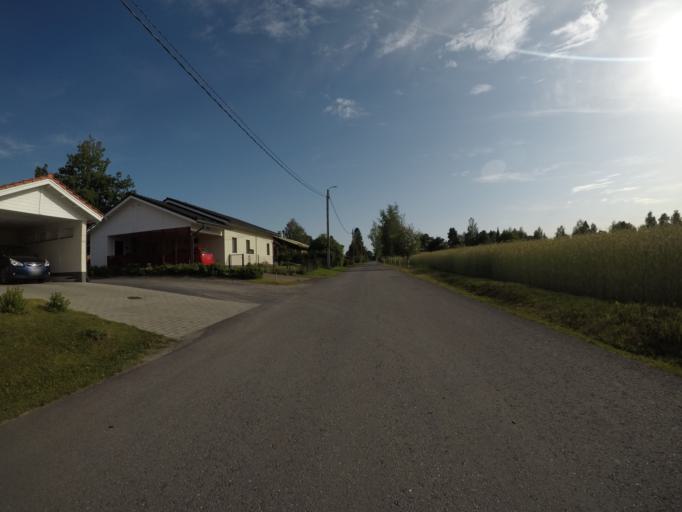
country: FI
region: Haeme
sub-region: Haemeenlinna
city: Haemeenlinna
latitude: 60.9796
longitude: 24.4215
